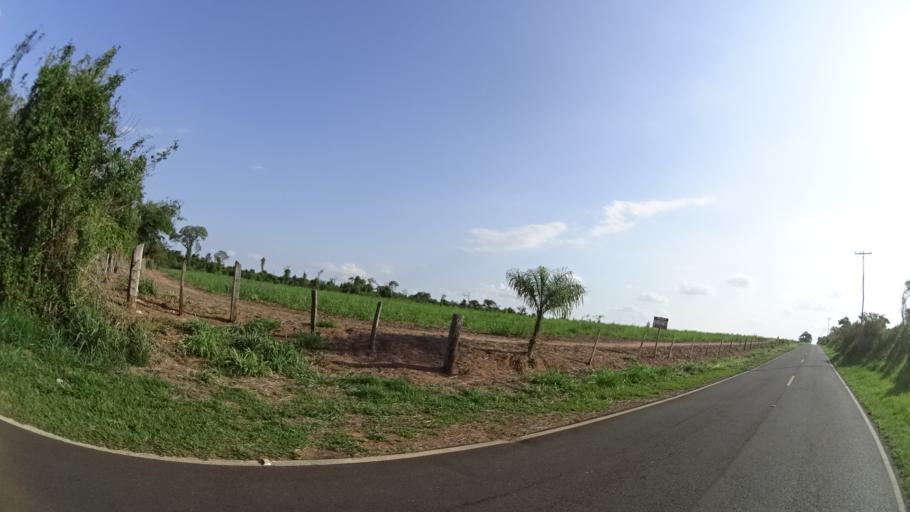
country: BR
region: Sao Paulo
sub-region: Urupes
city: Urupes
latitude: -21.3807
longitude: -49.4877
